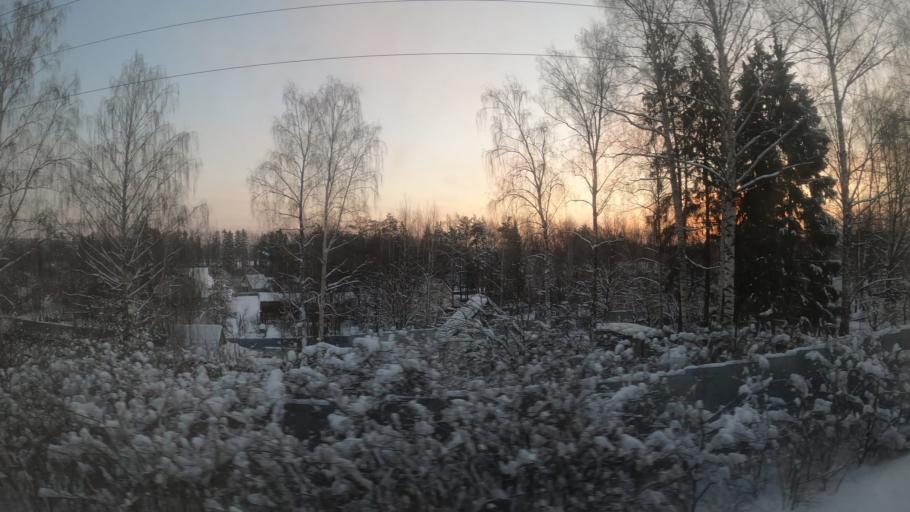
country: RU
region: Moskovskaya
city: Yermolino
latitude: 56.1433
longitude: 37.5065
